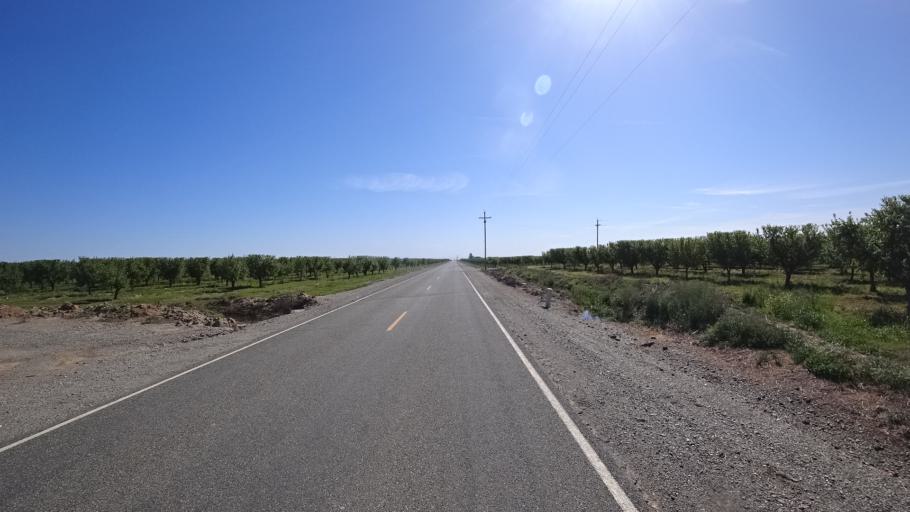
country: US
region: California
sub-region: Glenn County
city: Willows
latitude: 39.6240
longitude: -122.1696
